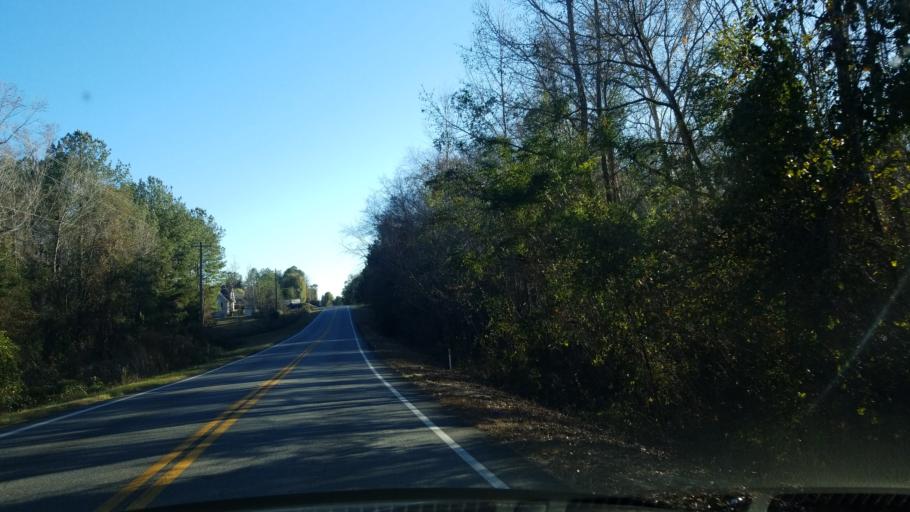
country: US
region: Georgia
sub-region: Talbot County
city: Talbotton
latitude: 32.5612
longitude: -84.6046
